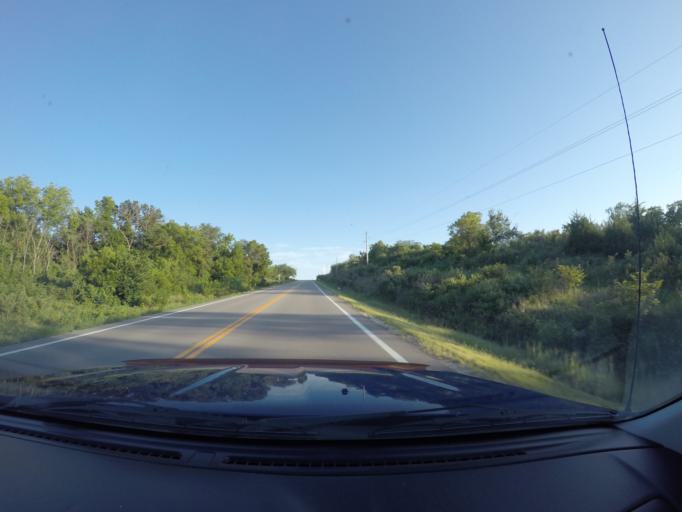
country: US
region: Kansas
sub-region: Pottawatomie County
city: Wamego
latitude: 39.1151
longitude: -96.2893
